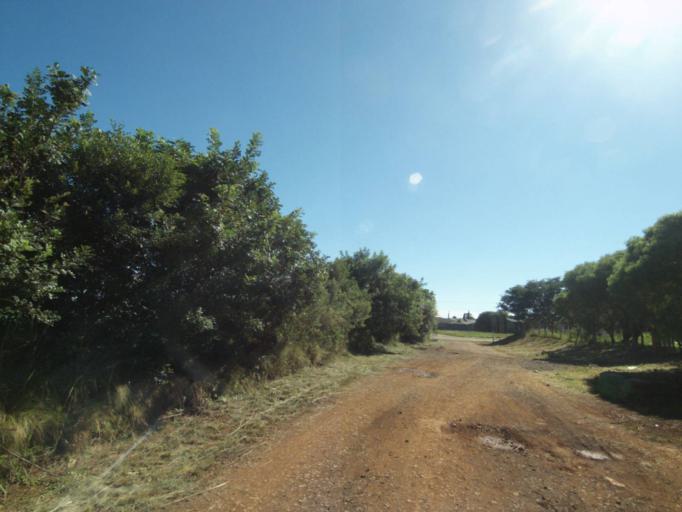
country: BR
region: Parana
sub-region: Pinhao
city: Pinhao
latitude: -25.8337
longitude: -52.0327
